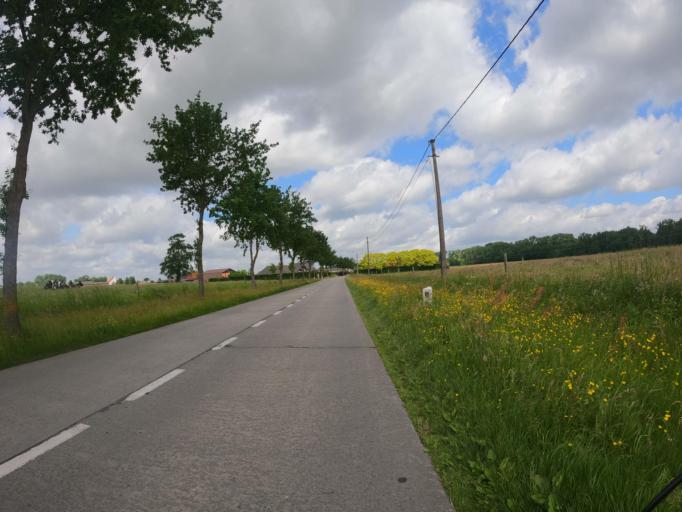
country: BE
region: Flanders
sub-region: Provincie West-Vlaanderen
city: Ruiselede
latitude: 51.0638
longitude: 3.3738
